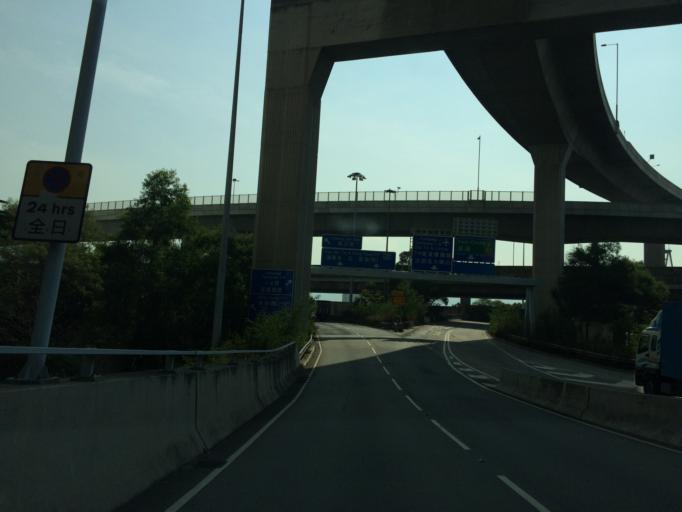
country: HK
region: Sham Shui Po
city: Sham Shui Po
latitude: 22.3323
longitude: 114.1449
